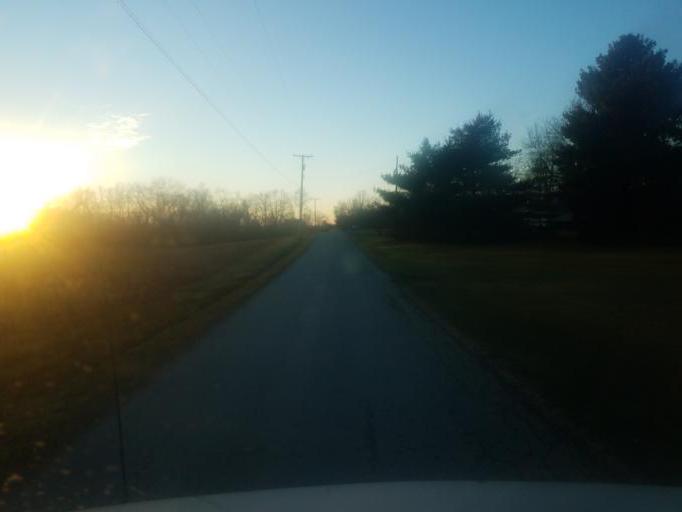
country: US
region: Ohio
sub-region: Richland County
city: Ontario
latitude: 40.8433
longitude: -82.5545
